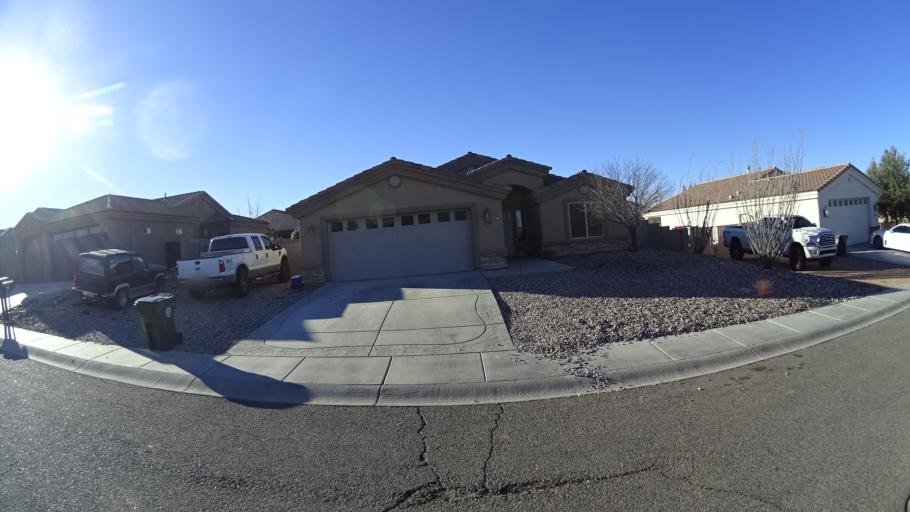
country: US
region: Arizona
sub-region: Mohave County
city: Kingman
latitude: 35.1937
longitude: -113.9987
